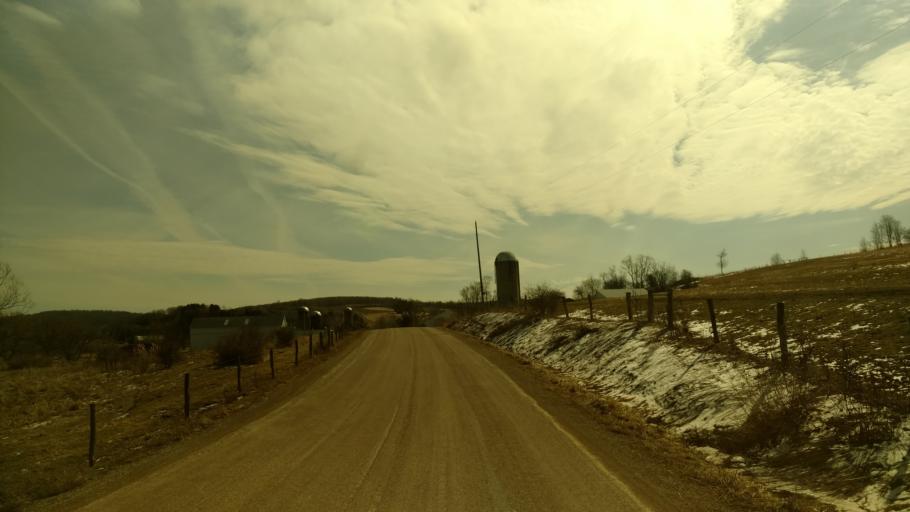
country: US
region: Pennsylvania
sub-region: Tioga County
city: Westfield
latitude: 41.9218
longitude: -77.7552
